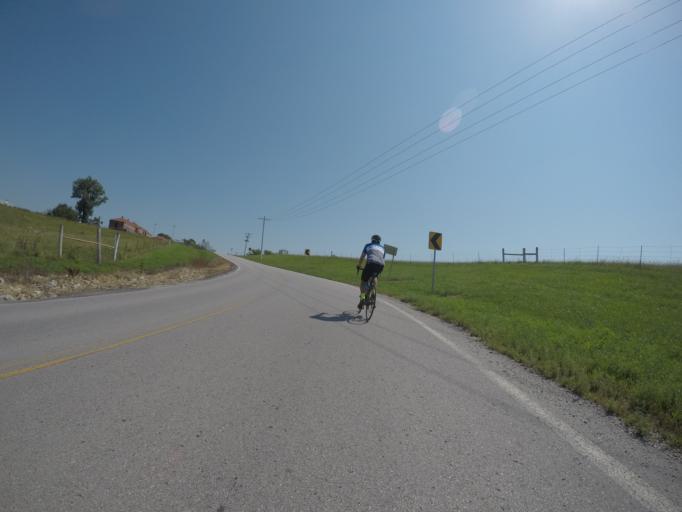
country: US
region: Kansas
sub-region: Leavenworth County
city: Lansing
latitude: 39.2561
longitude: -94.8812
